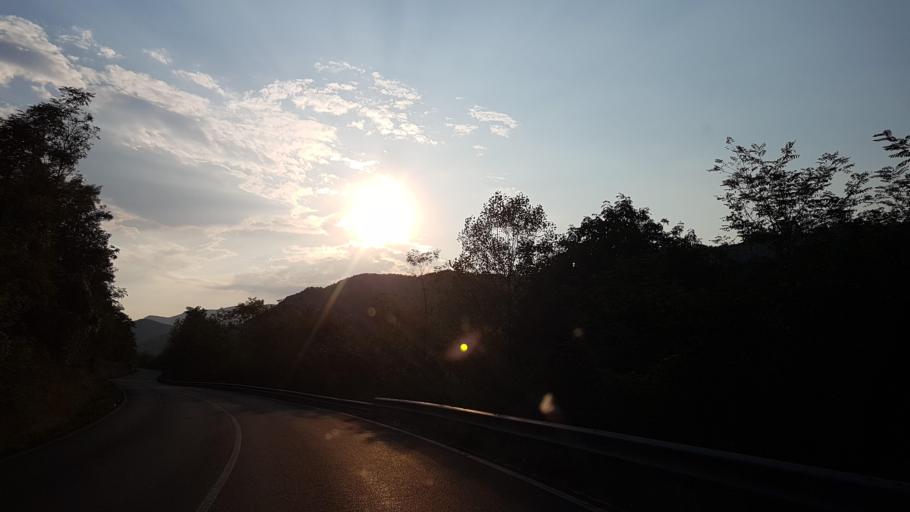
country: IT
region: Emilia-Romagna
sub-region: Provincia di Parma
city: Stazione Valmozzola
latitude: 44.5400
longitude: 9.8919
